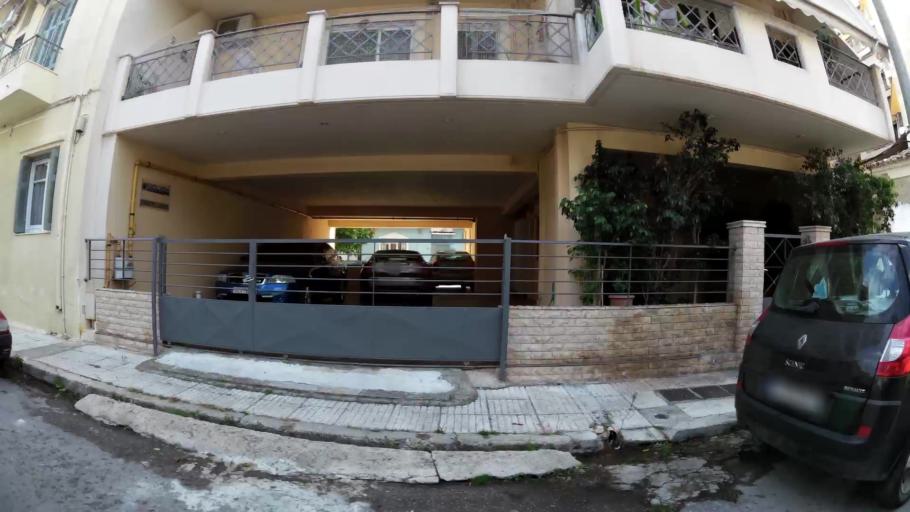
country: GR
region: Attica
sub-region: Nomarchia Athinas
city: Athens
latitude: 37.9940
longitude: 23.7094
